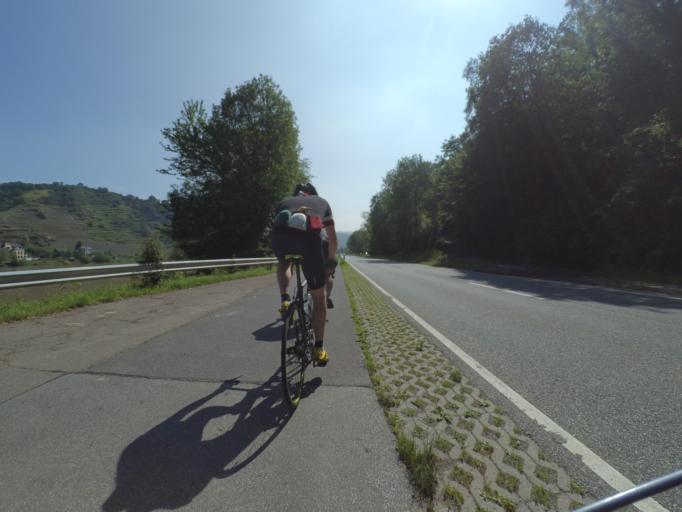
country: DE
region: Rheinland-Pfalz
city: Hatzenport
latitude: 50.2255
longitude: 7.4213
